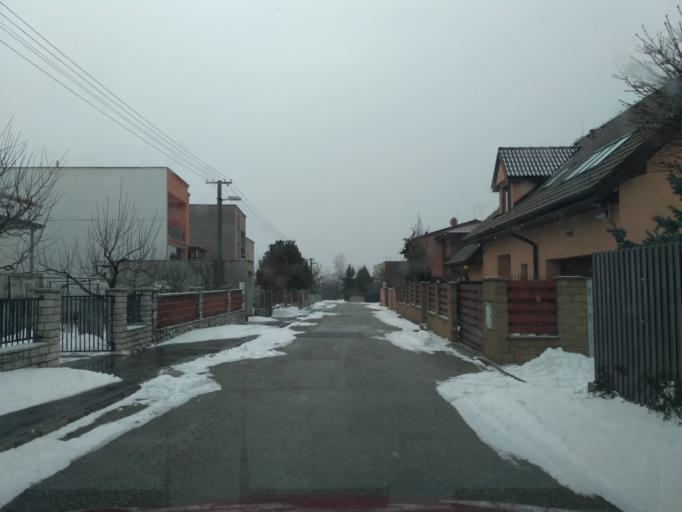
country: SK
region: Kosicky
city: Kosice
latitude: 48.7183
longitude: 21.2218
